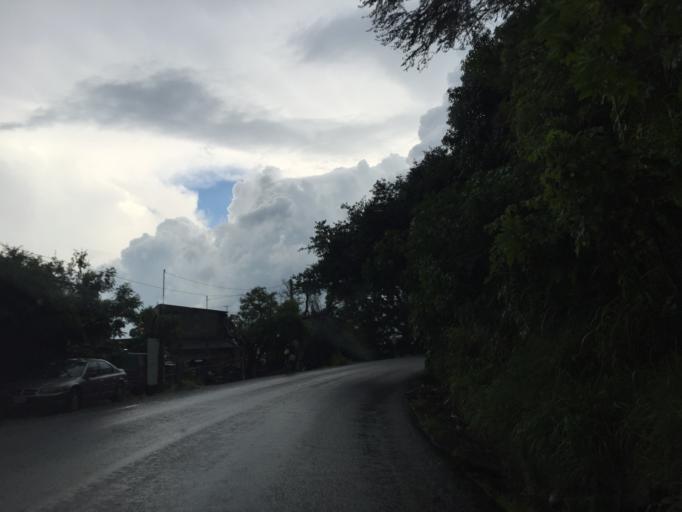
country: MX
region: Colima
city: Queseria
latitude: 19.3891
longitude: -103.5666
